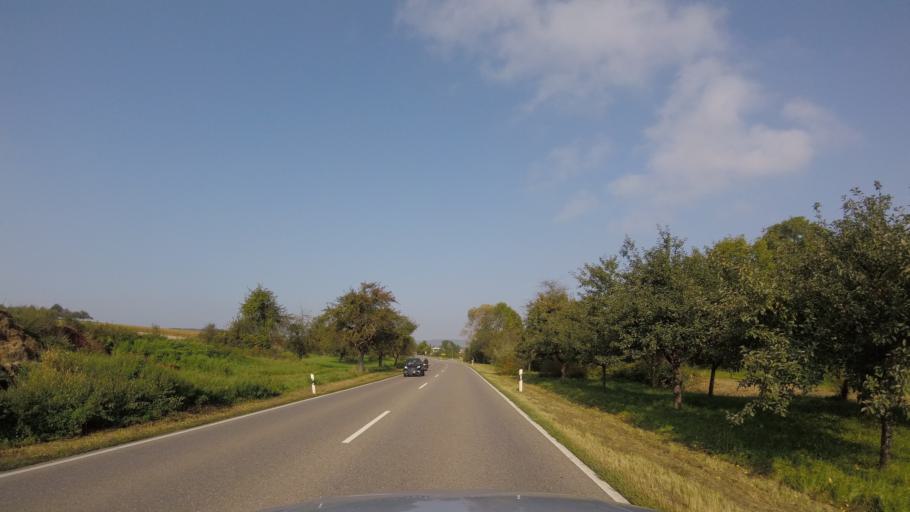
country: DE
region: Baden-Wuerttemberg
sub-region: Regierungsbezirk Stuttgart
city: Grossbottwar
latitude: 48.9926
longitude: 9.3025
